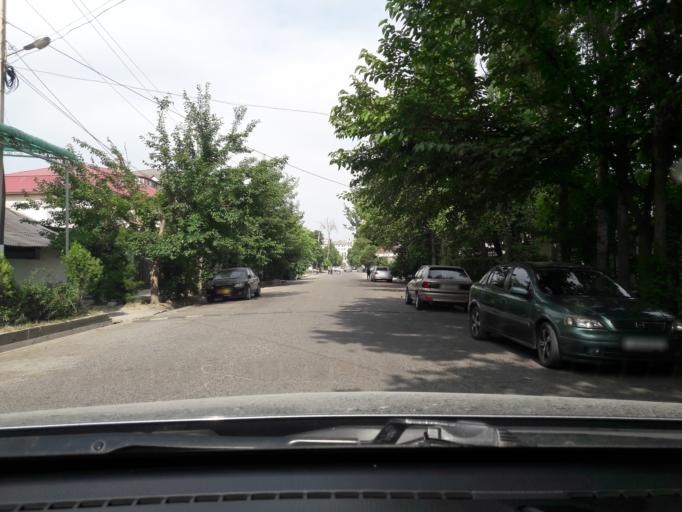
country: TJ
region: Dushanbe
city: Dushanbe
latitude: 38.5381
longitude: 68.7565
